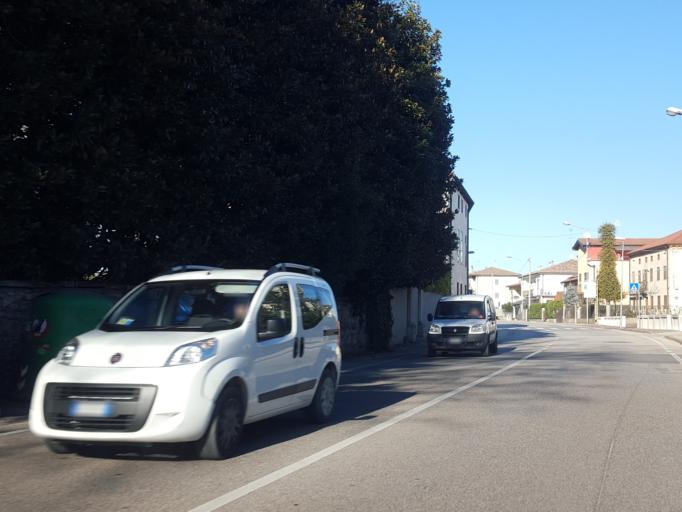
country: IT
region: Veneto
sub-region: Provincia di Vicenza
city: Vicenza
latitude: 45.5236
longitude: 11.5637
